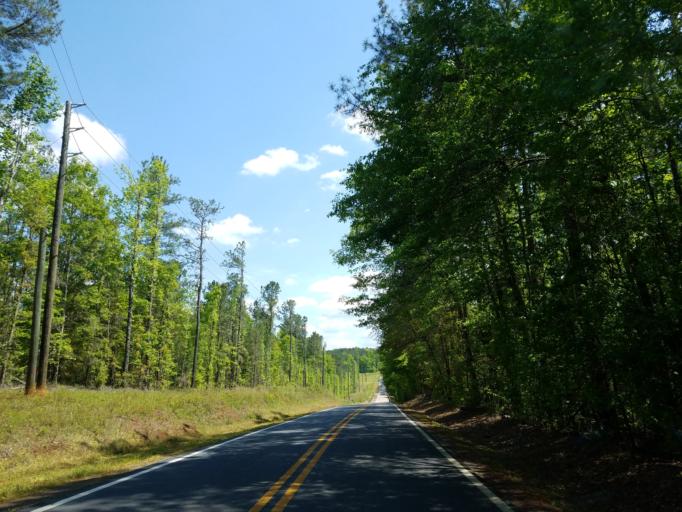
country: US
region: Georgia
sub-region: Monroe County
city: Forsyth
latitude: 33.1309
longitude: -83.9724
